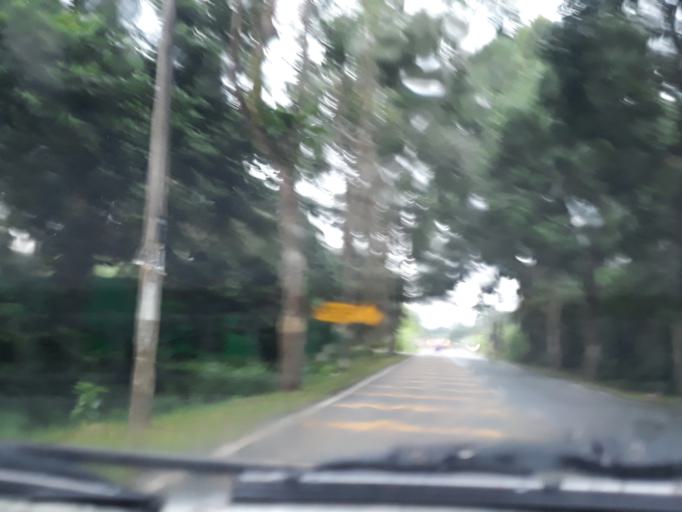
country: MY
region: Penang
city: Nibong Tebal
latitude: 5.2230
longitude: 100.6078
